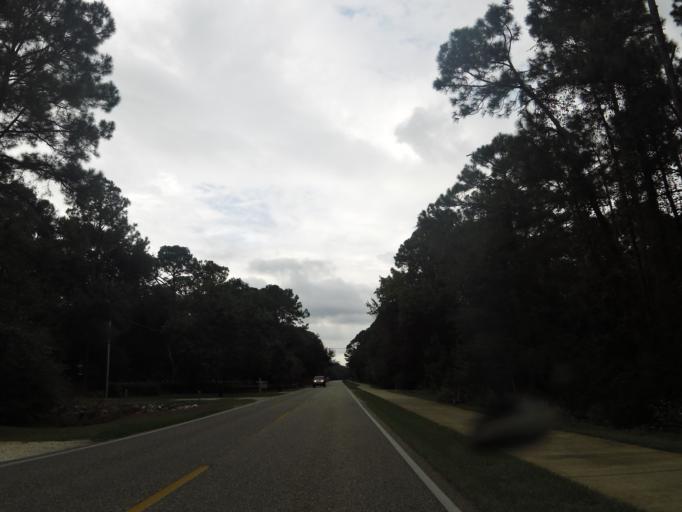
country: US
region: Alabama
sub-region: Baldwin County
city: Point Clear
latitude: 30.4325
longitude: -87.9108
